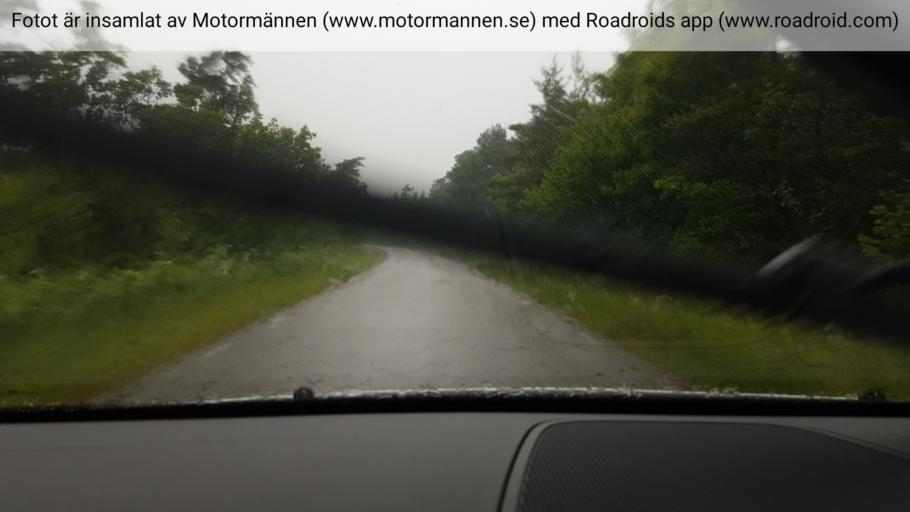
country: SE
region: Gotland
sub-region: Gotland
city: Slite
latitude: 57.8961
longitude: 18.7115
